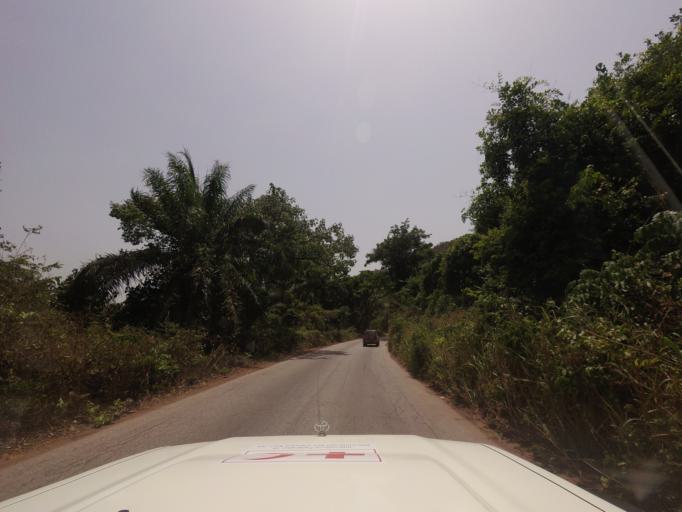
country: GN
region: Kindia
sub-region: Coyah
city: Coyah
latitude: 9.7425
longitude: -13.3666
